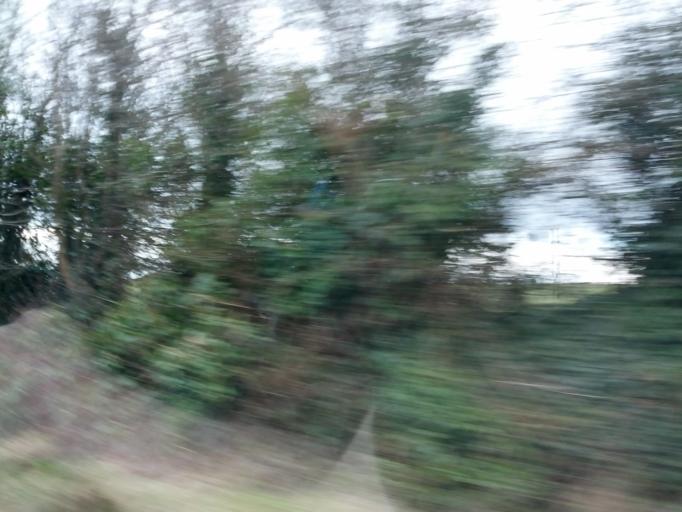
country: IE
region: Connaught
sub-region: County Galway
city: Athenry
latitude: 53.4564
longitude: -8.5829
